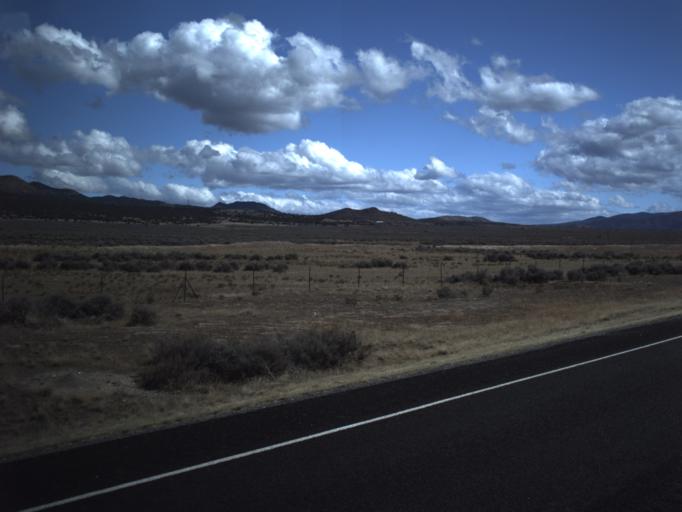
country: US
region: Utah
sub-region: Beaver County
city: Milford
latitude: 38.2842
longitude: -112.9652
